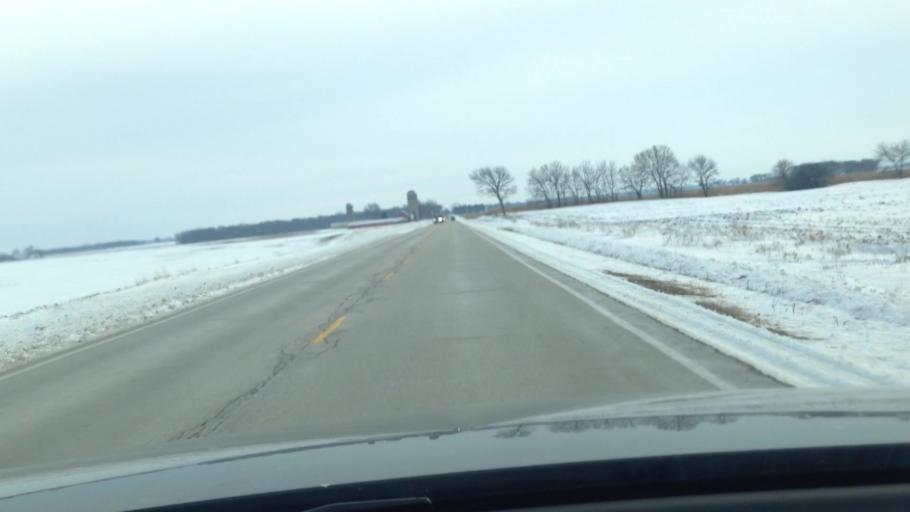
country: US
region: Illinois
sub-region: McHenry County
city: Hebron
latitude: 42.4346
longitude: -88.4381
